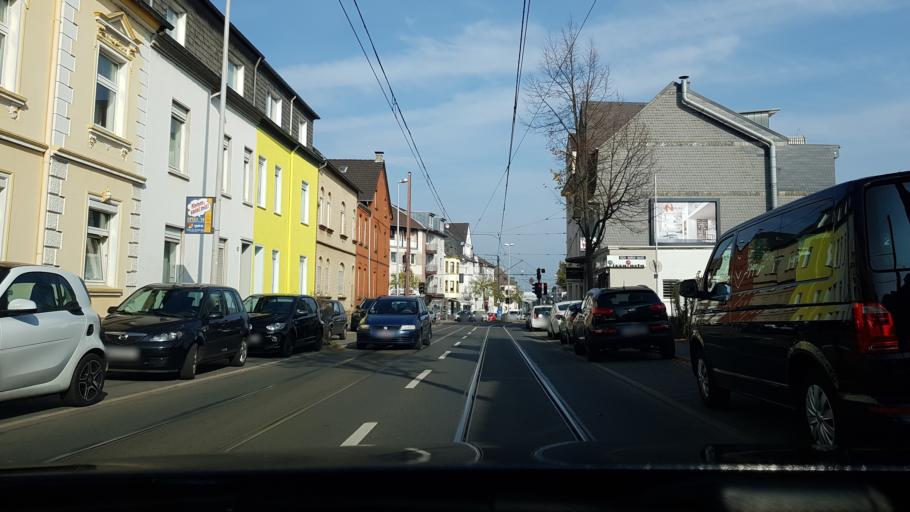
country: DE
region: North Rhine-Westphalia
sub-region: Regierungsbezirk Dusseldorf
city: Muelheim (Ruhr)
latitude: 51.4233
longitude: 6.8614
